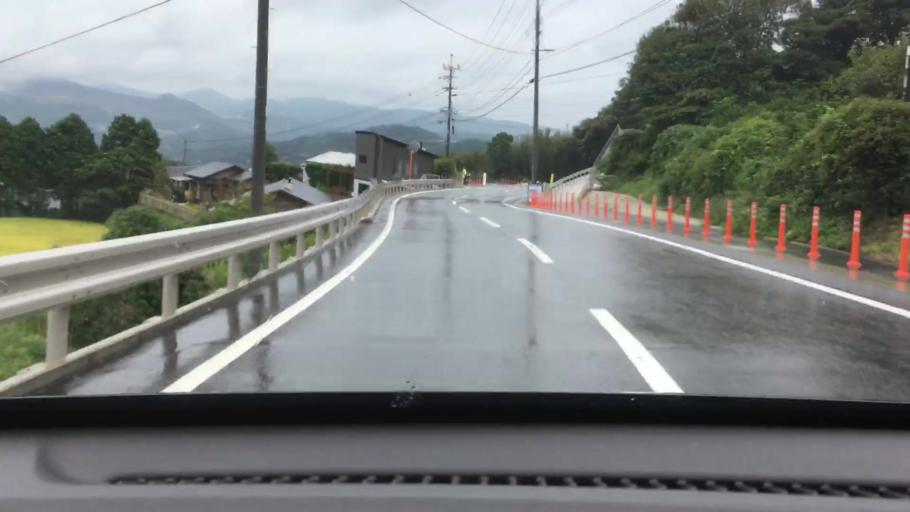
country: JP
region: Nagasaki
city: Togitsu
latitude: 32.8693
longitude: 129.7667
